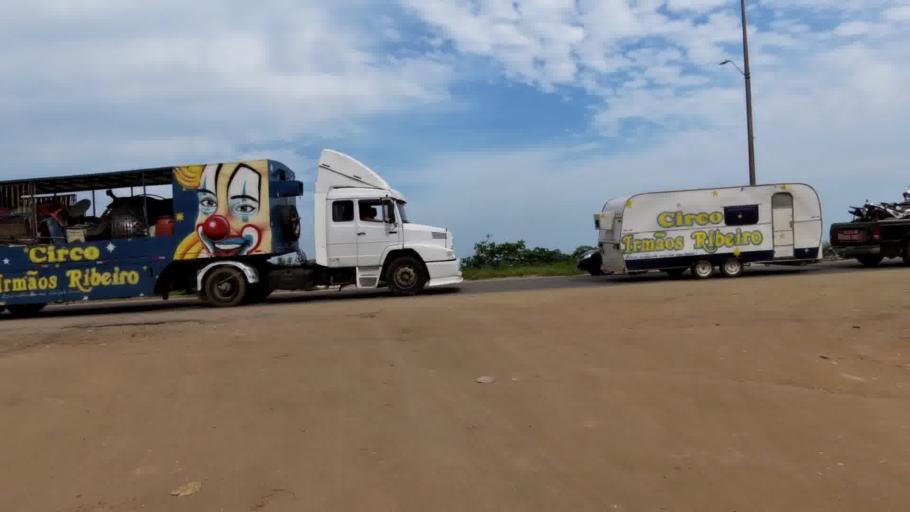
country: BR
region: Espirito Santo
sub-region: Piuma
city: Piuma
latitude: -20.8432
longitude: -40.7327
